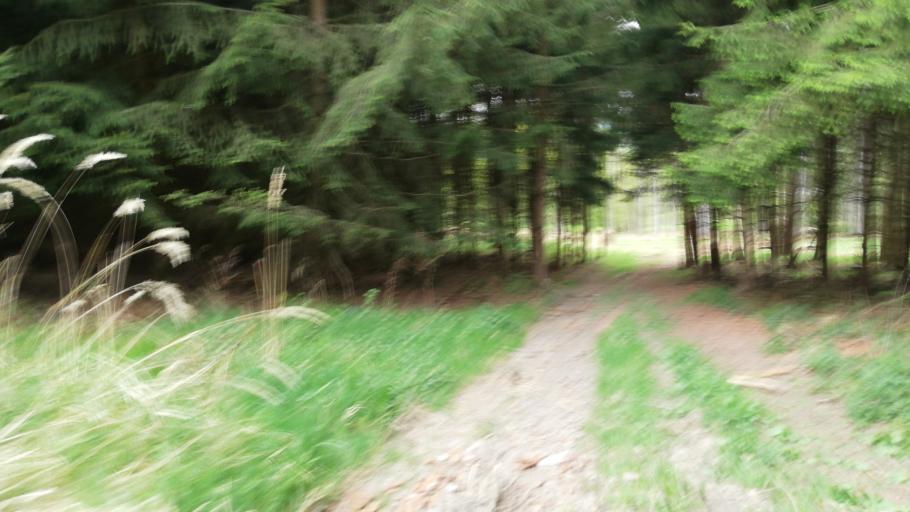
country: AT
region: Upper Austria
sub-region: Politischer Bezirk Grieskirchen
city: Bad Schallerbach
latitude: 48.1872
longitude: 13.9322
